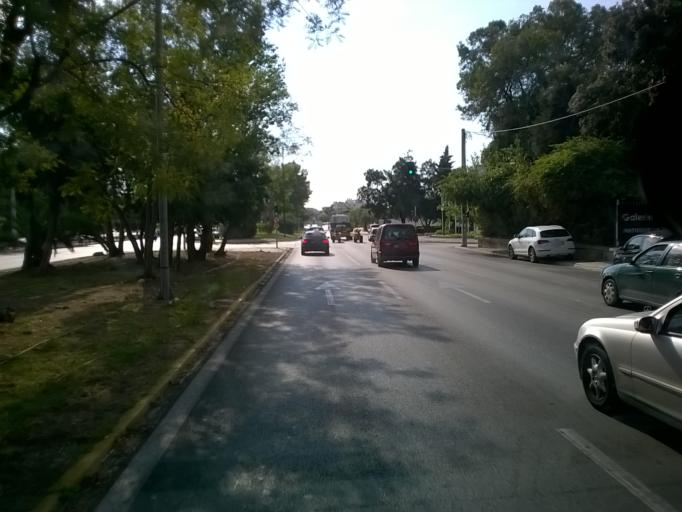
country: GR
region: Attica
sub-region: Nomarchia Athinas
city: Glyfada
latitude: 37.8651
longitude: 23.7443
